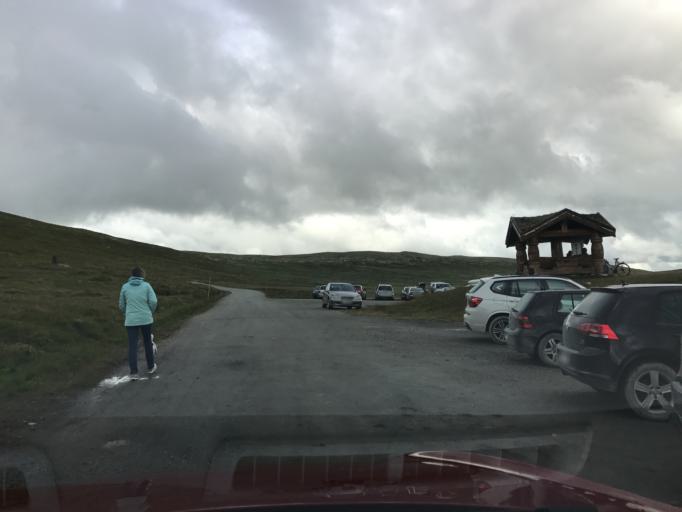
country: NO
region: Buskerud
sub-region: Hol
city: Geilo
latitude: 60.5492
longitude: 8.0687
